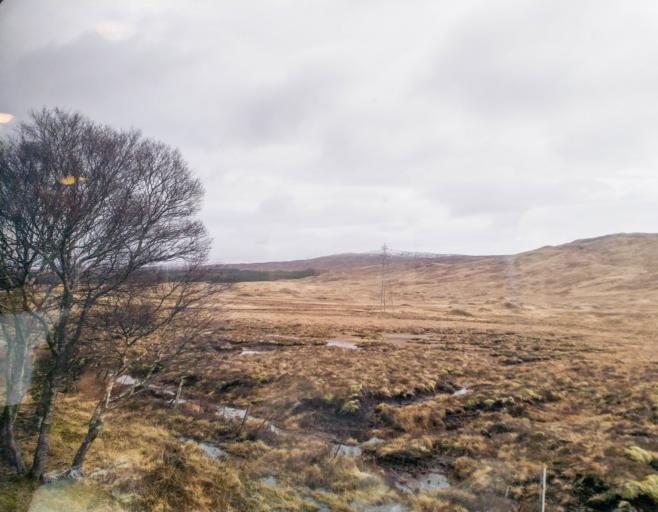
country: GB
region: Scotland
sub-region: Highland
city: Spean Bridge
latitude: 56.5987
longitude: -4.6104
